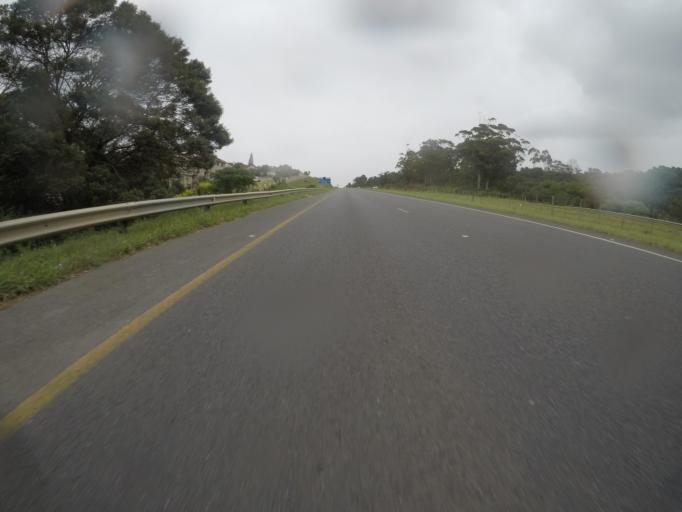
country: ZA
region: Eastern Cape
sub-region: Buffalo City Metropolitan Municipality
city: East London
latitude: -32.9480
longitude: 27.9382
